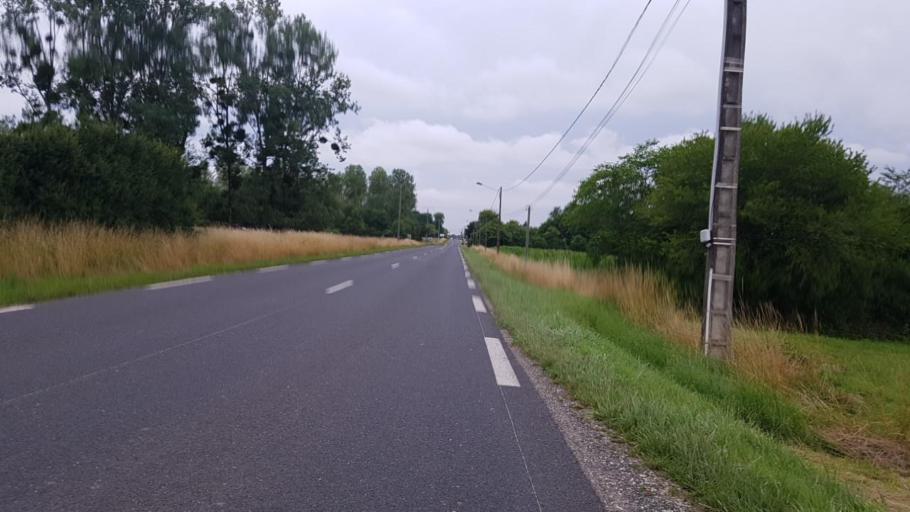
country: FR
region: Champagne-Ardenne
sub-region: Departement de la Marne
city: Pargny-sur-Saulx
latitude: 48.7732
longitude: 4.8646
